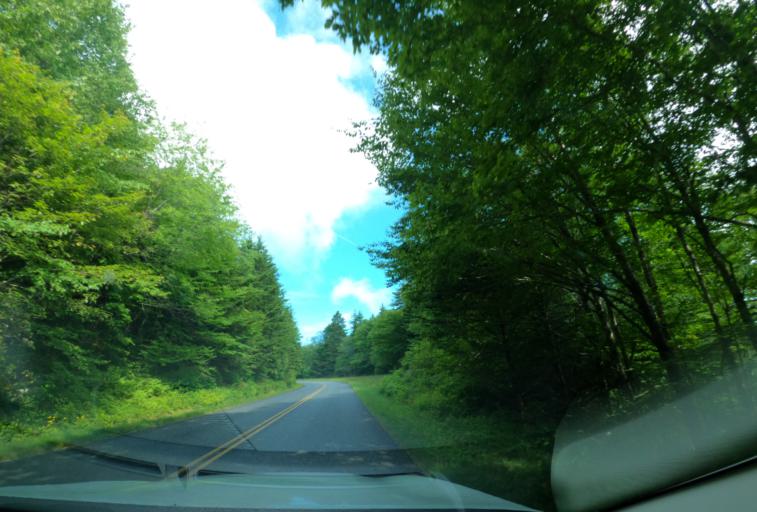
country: US
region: North Carolina
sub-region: Haywood County
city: Hazelwood
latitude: 35.3181
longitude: -82.9585
